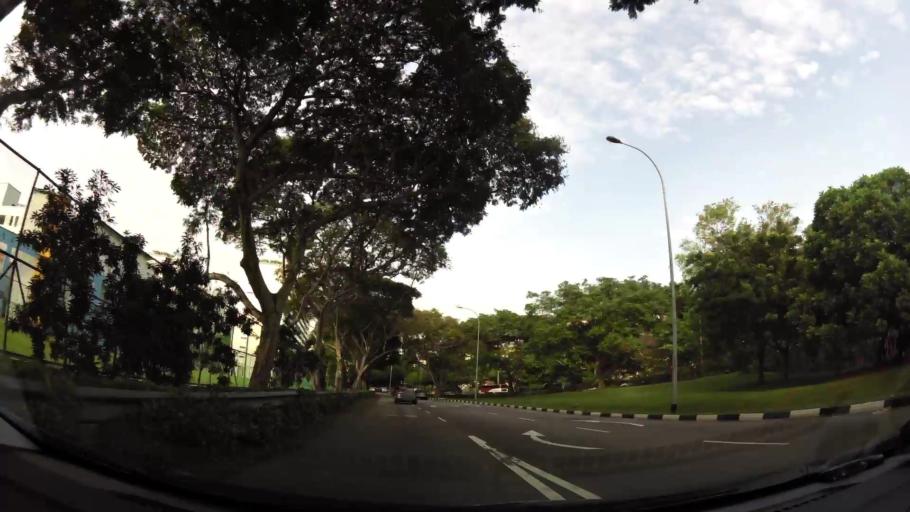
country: SG
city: Singapore
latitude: 1.3254
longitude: 103.9047
